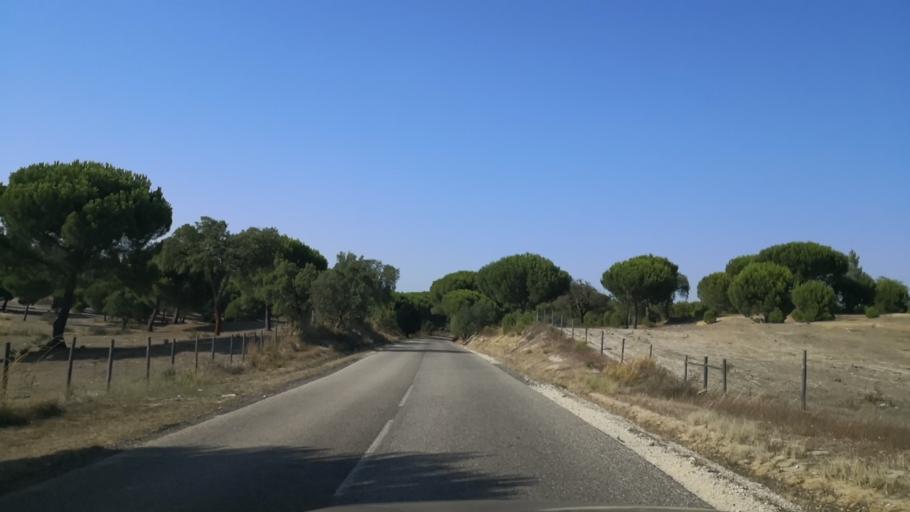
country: PT
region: Santarem
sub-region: Coruche
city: Coruche
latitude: 38.8599
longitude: -8.5445
